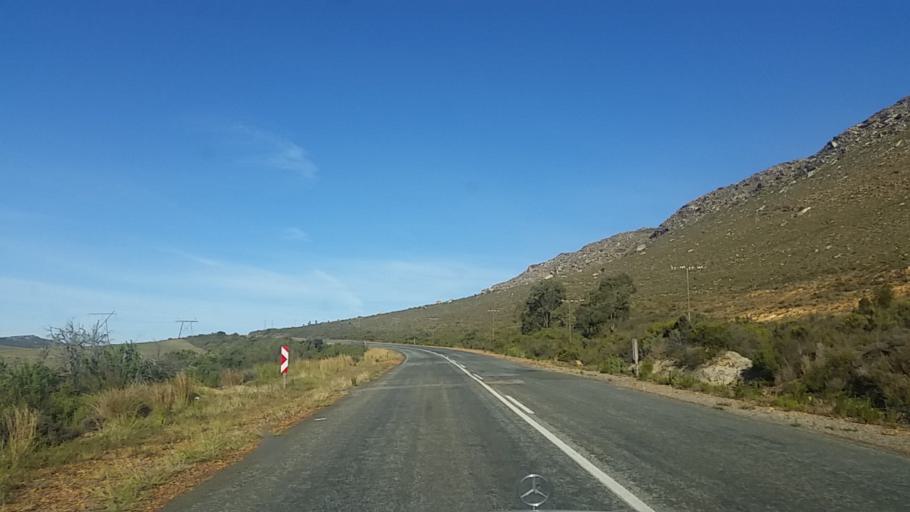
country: ZA
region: Western Cape
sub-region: Eden District Municipality
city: Knysna
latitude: -33.7429
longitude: 23.0203
